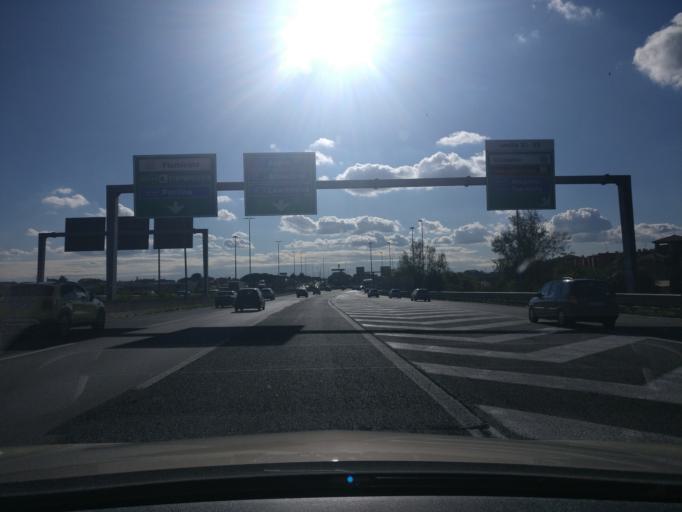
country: IT
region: Latium
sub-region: Citta metropolitana di Roma Capitale
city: Ciampino
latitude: 41.8365
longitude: 12.5894
